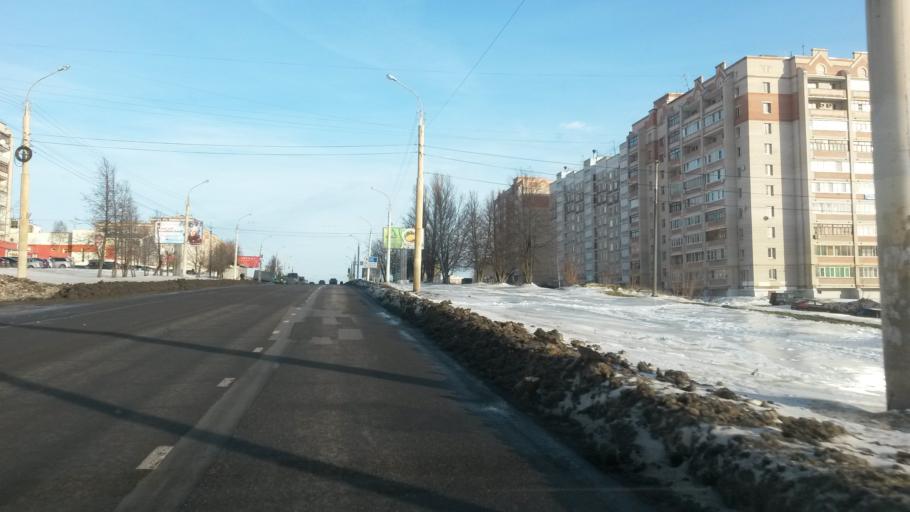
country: RU
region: Kostroma
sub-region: Kostromskoy Rayon
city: Kostroma
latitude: 57.7337
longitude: 40.9070
